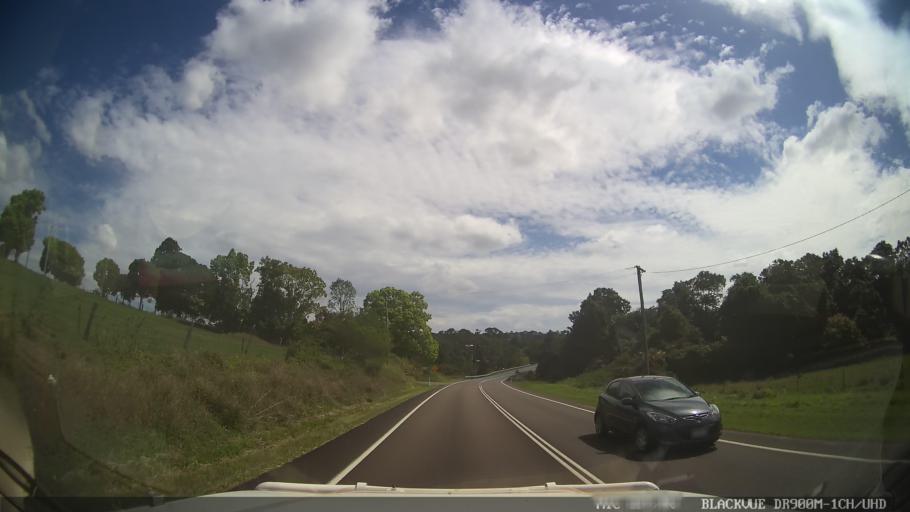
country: AU
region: Queensland
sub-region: Sunshine Coast
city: Nambour
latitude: -26.6190
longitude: 152.8866
